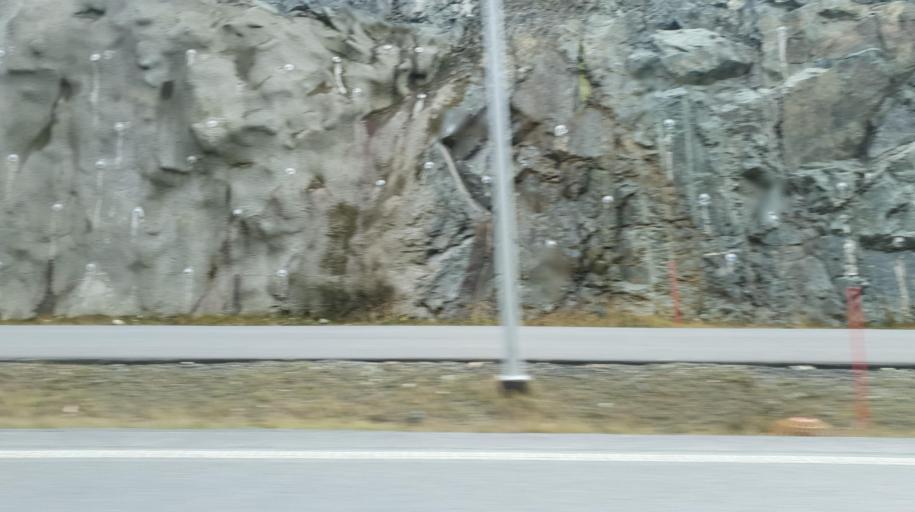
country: NO
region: Sor-Trondelag
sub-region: Klaebu
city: Klaebu
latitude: 63.3174
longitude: 10.3963
